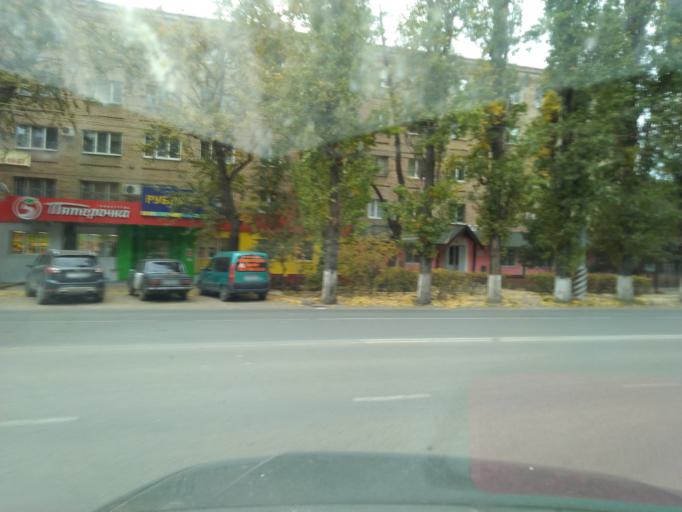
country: RU
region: Saratov
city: Engel's
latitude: 51.4737
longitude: 46.1328
